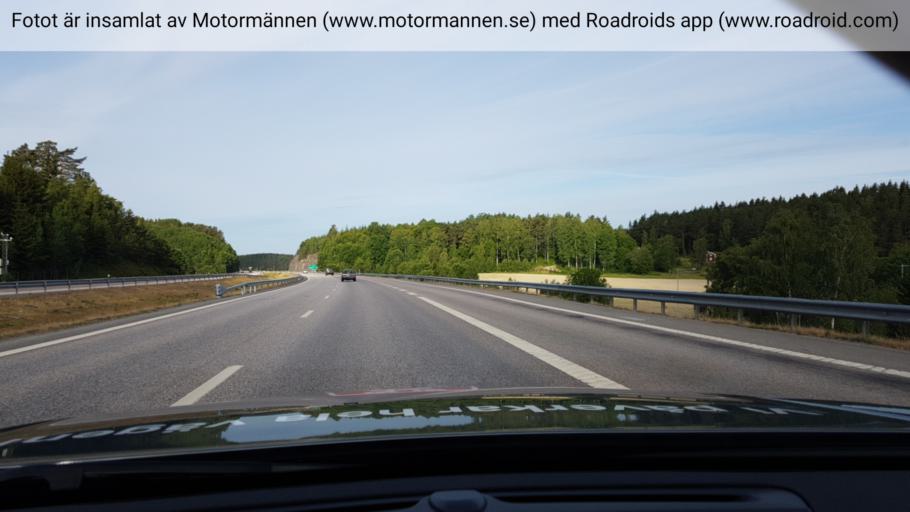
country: SE
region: Soedermanland
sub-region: Gnesta Kommun
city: Gnesta
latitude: 58.9089
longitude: 17.3318
